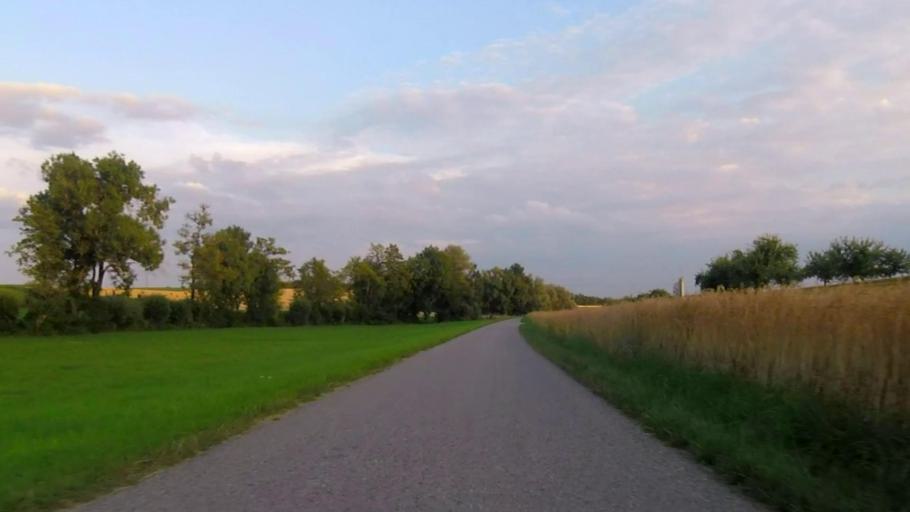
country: DE
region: Baden-Wuerttemberg
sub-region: Regierungsbezirk Stuttgart
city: Aspach
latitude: 48.9655
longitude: 9.3749
